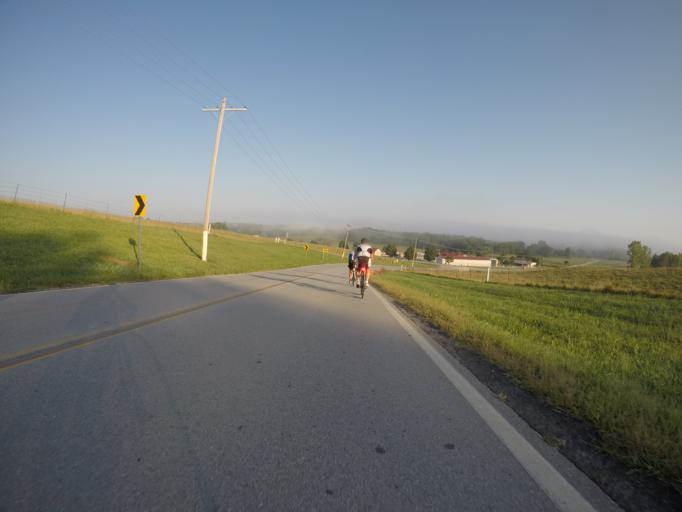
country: US
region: Kansas
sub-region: Leavenworth County
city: Lansing
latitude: 39.2556
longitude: -94.8805
